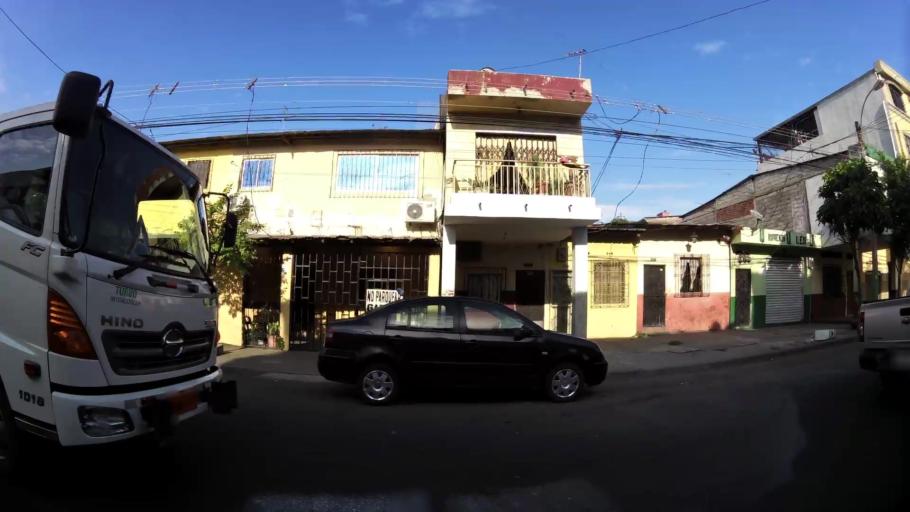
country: EC
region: Guayas
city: Guayaquil
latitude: -2.2141
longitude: -79.9021
